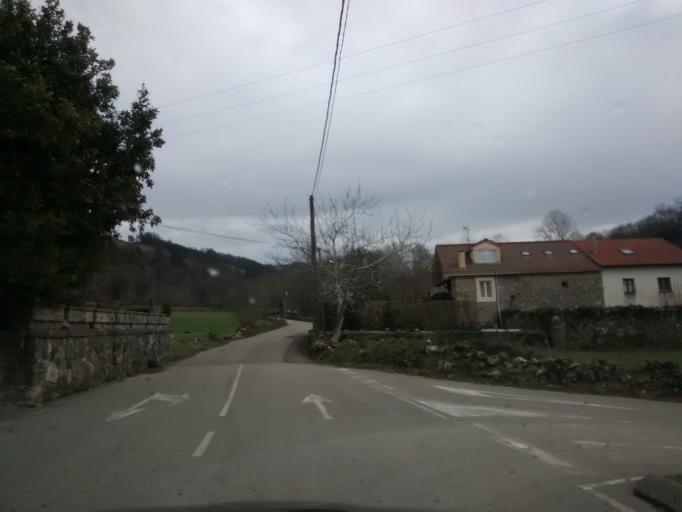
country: ES
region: Cantabria
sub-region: Provincia de Cantabria
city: Entrambasaguas
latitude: 43.3448
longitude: -3.6932
